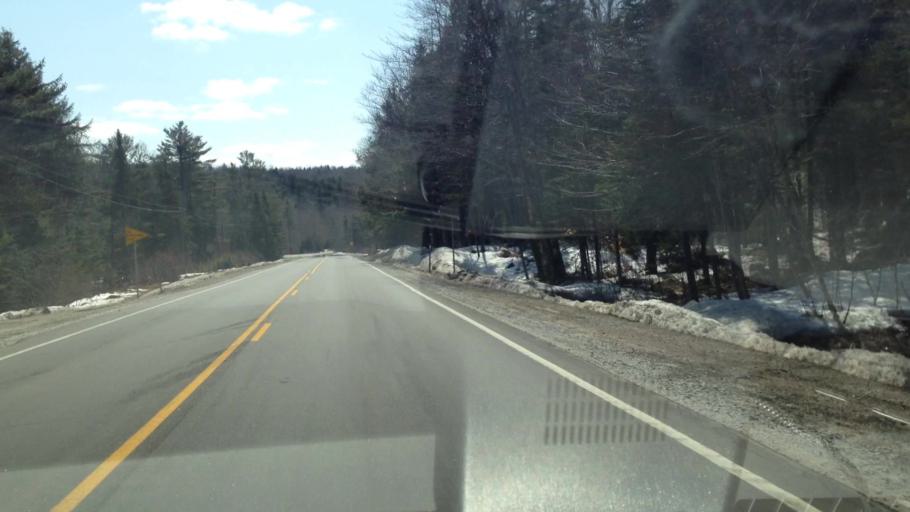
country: US
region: New Hampshire
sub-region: Merrimack County
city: Wilmot
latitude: 43.4676
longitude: -71.9602
